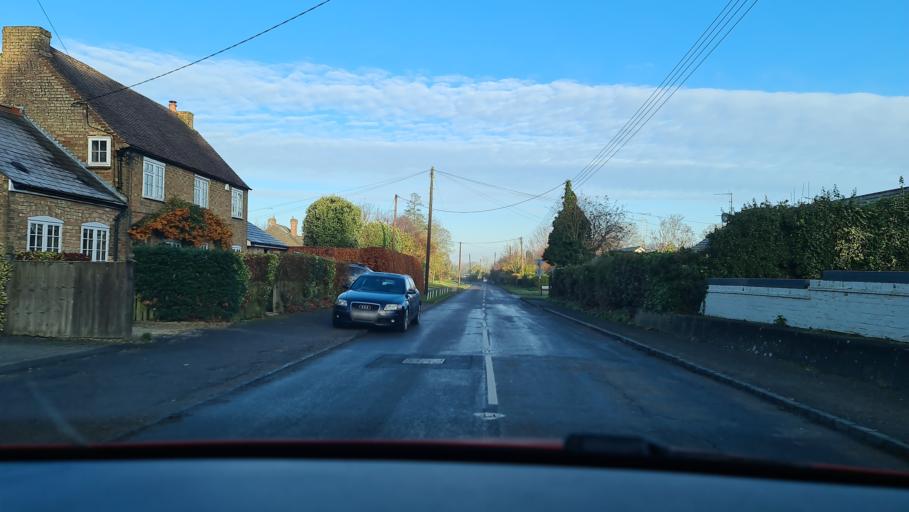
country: GB
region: England
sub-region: Buckinghamshire
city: Wendover
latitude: 51.7560
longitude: -0.7806
